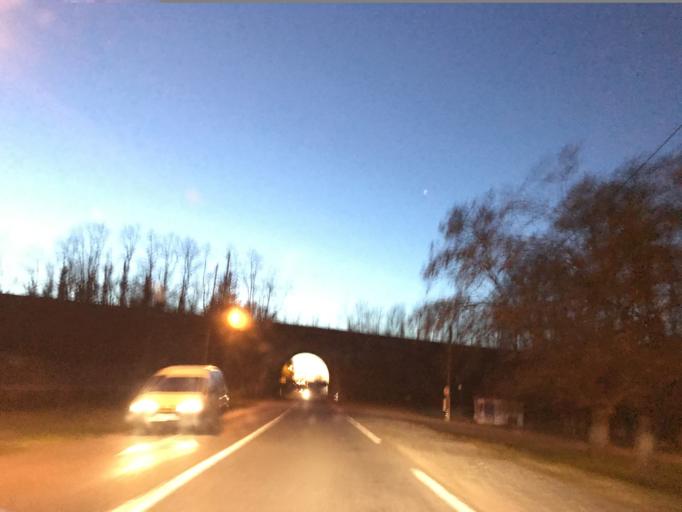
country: FR
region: Auvergne
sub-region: Departement de l'Allier
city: Hauterive
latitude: 46.0917
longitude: 3.4416
